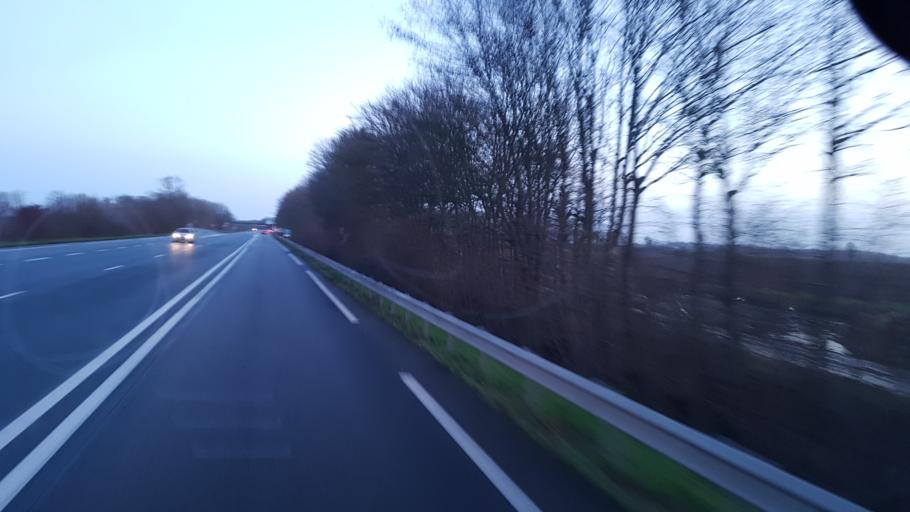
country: FR
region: Nord-Pas-de-Calais
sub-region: Departement du Nord
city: Ferin
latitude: 50.3386
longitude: 3.0847
